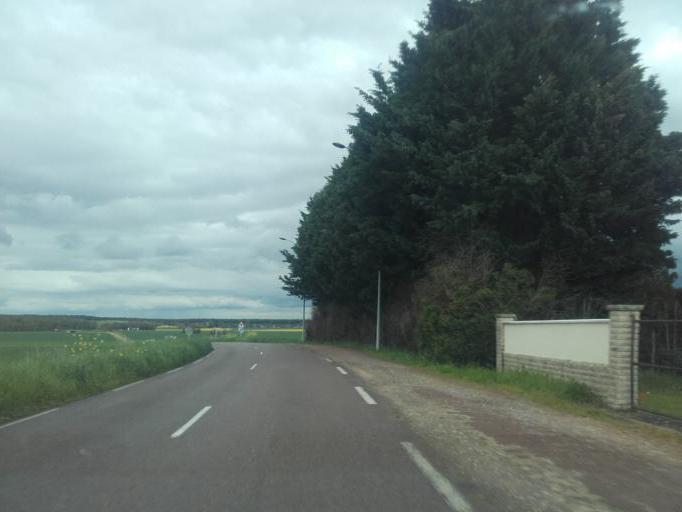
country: FR
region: Bourgogne
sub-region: Departement de la Cote-d'Or
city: Beaune
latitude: 47.0412
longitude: 4.8727
